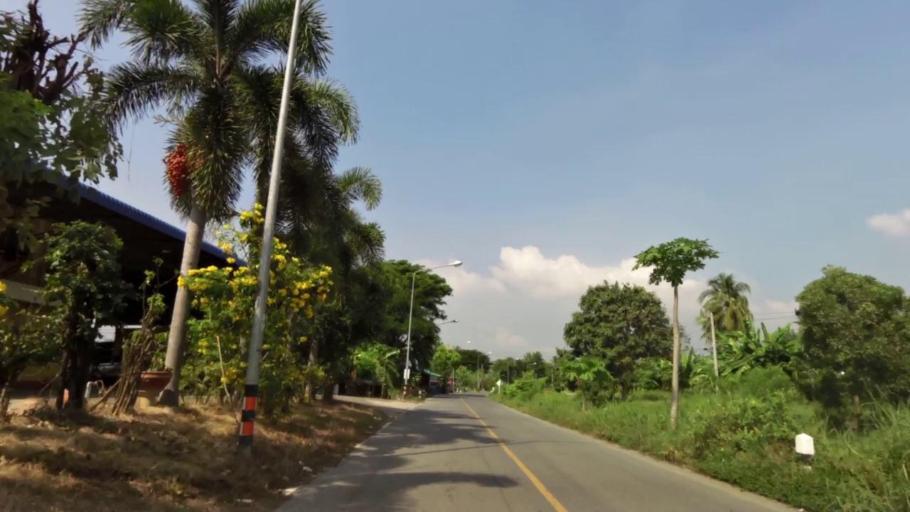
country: TH
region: Ang Thong
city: Ang Thong
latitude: 14.5998
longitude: 100.4007
